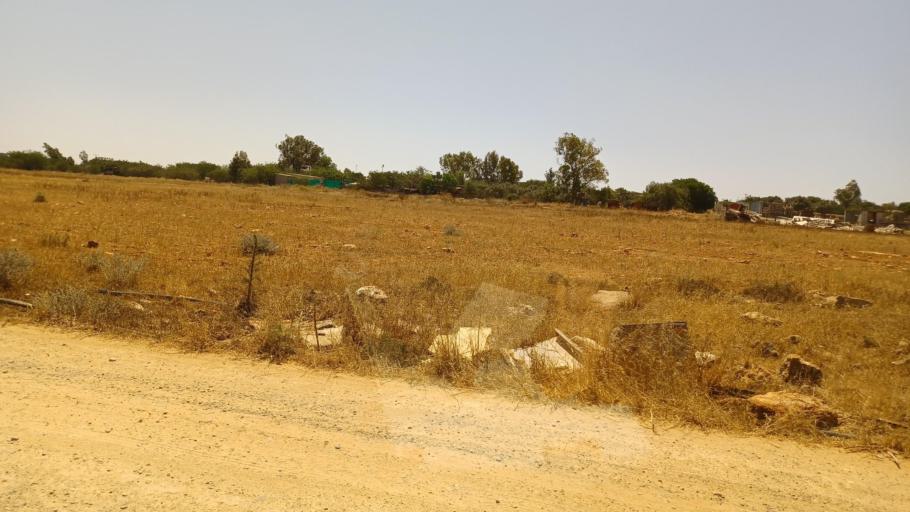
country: CY
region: Ammochostos
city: Liopetri
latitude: 35.0283
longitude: 33.8885
